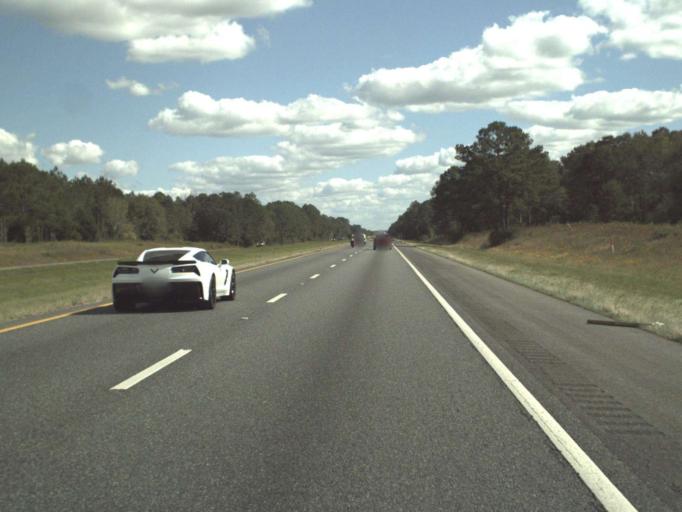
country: US
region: Florida
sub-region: Jackson County
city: Marianna
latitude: 30.7116
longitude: -85.1554
